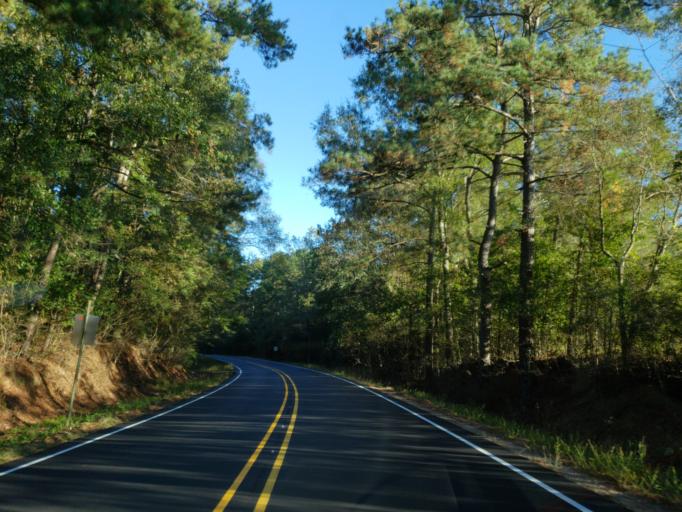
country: US
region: Mississippi
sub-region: Perry County
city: Richton
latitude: 31.3509
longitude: -88.7852
